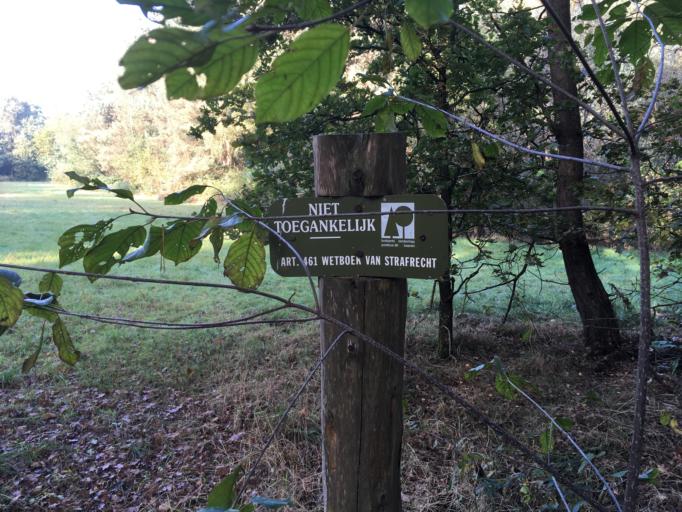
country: NL
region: North Brabant
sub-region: Gemeente Vught
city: Vught
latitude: 51.6266
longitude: 5.2670
